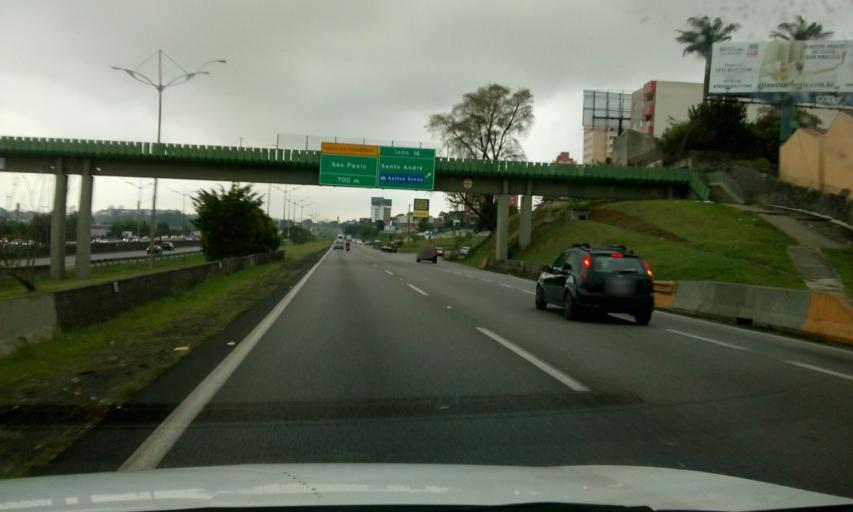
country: BR
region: Sao Paulo
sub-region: Sao Bernardo Do Campo
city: Sao Bernardo do Campo
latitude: -23.6695
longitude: -46.5717
